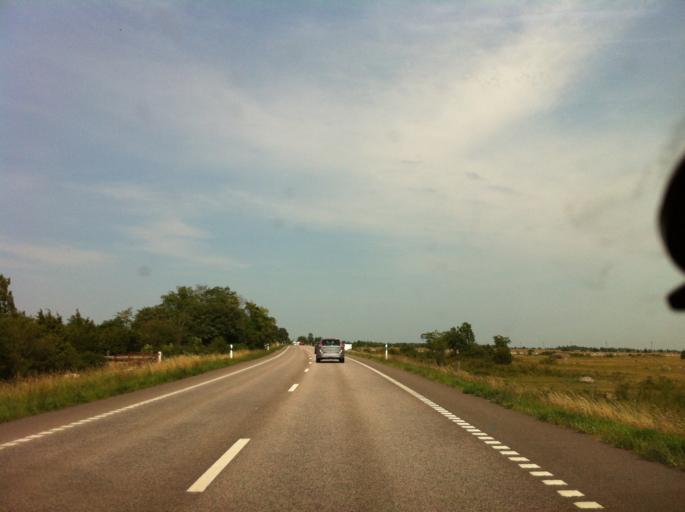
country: SE
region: Kalmar
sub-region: Borgholms Kommun
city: Borgholm
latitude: 56.8257
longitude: 16.6105
